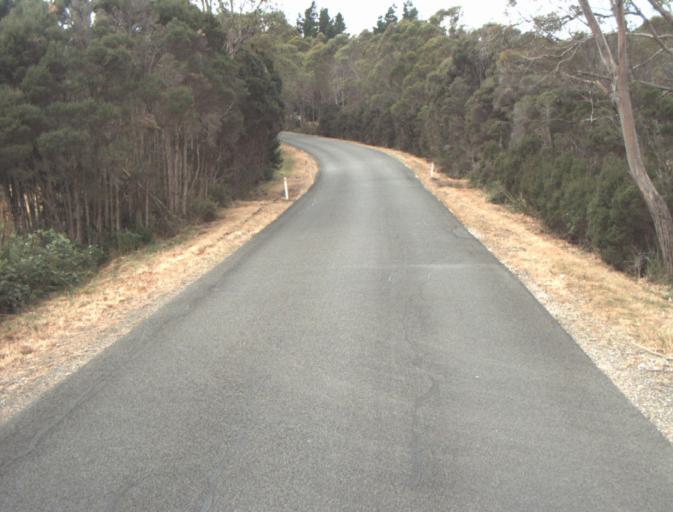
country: AU
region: Tasmania
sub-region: Launceston
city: Mayfield
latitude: -41.2232
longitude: 147.0442
